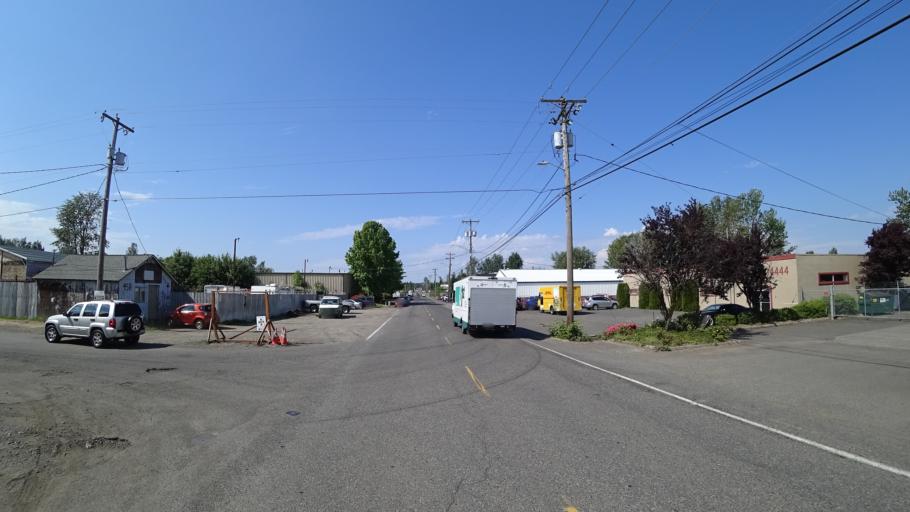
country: US
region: Oregon
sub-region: Multnomah County
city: Fairview
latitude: 45.5553
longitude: -122.5103
